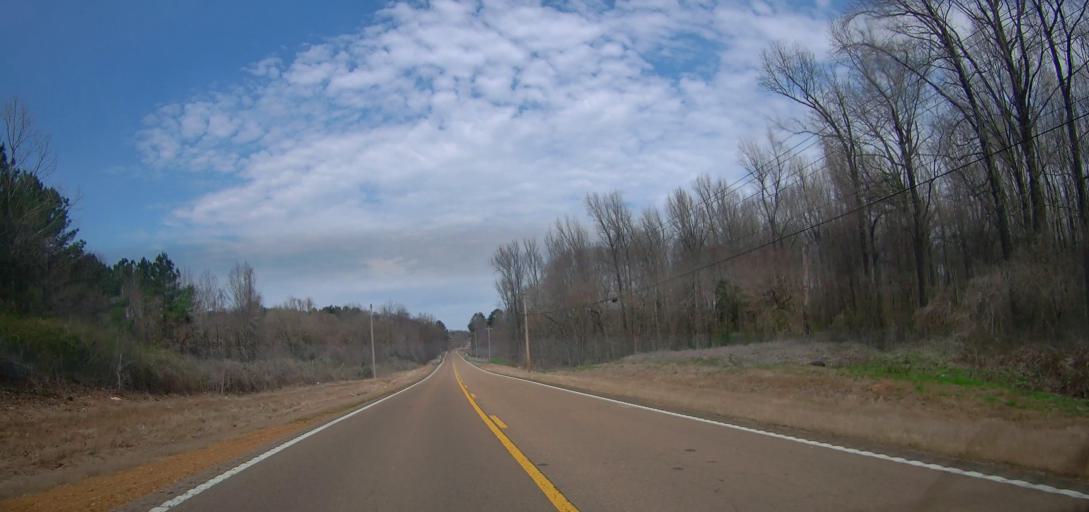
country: US
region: Mississippi
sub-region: Marshall County
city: Holly Springs
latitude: 34.7214
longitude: -89.4145
